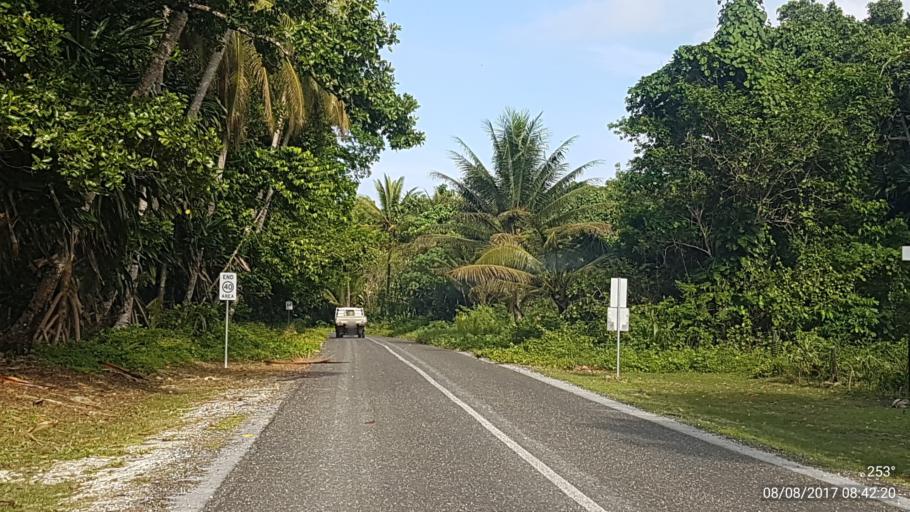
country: PG
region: Manus
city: Lorengau
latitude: -2.0793
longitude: 147.4028
